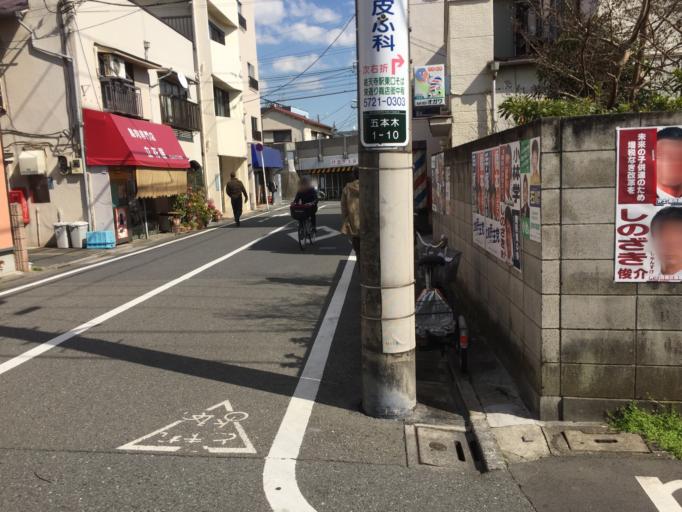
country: JP
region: Tokyo
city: Tokyo
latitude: 35.6393
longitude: 139.6918
